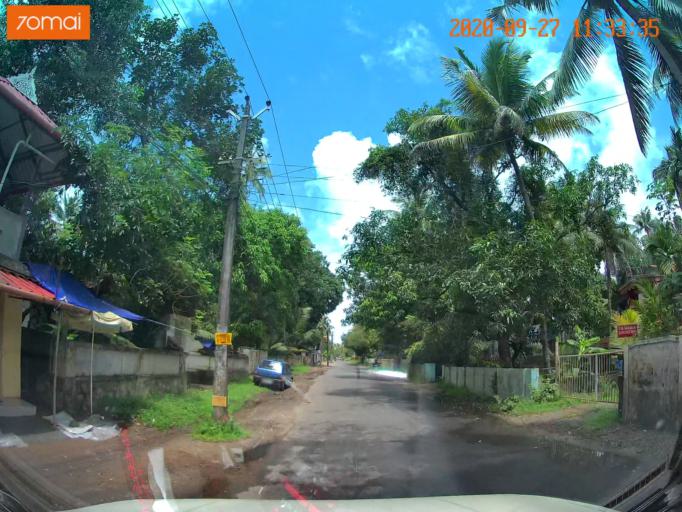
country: IN
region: Kerala
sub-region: Thrissur District
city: Thanniyam
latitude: 10.4319
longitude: 76.1288
